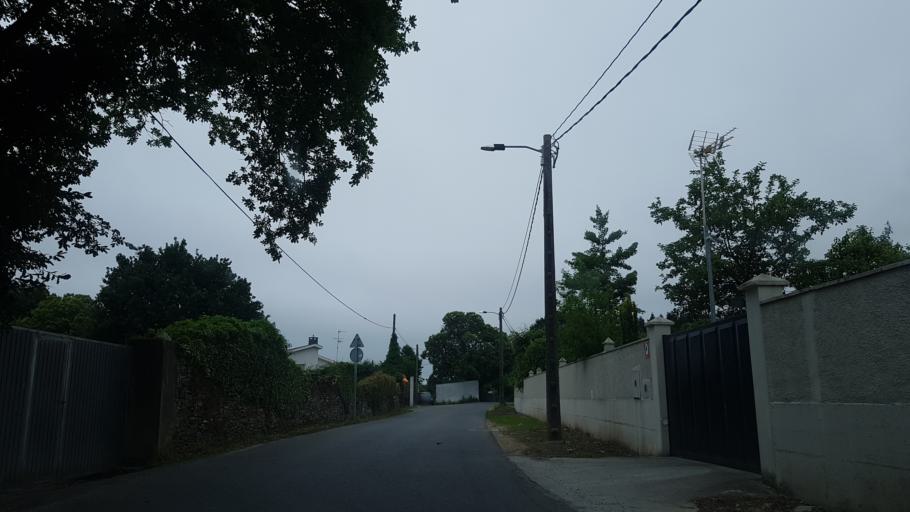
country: ES
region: Galicia
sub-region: Provincia de Lugo
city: Lugo
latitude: 43.0358
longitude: -7.5599
